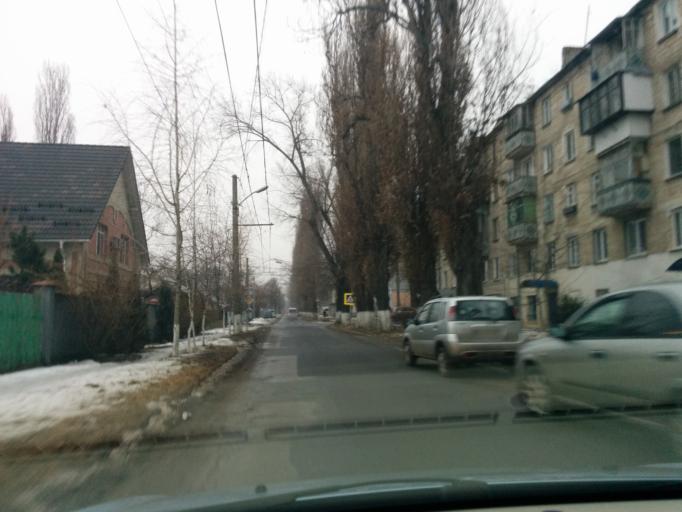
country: MD
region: Chisinau
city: Chisinau
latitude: 46.9991
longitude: 28.8627
